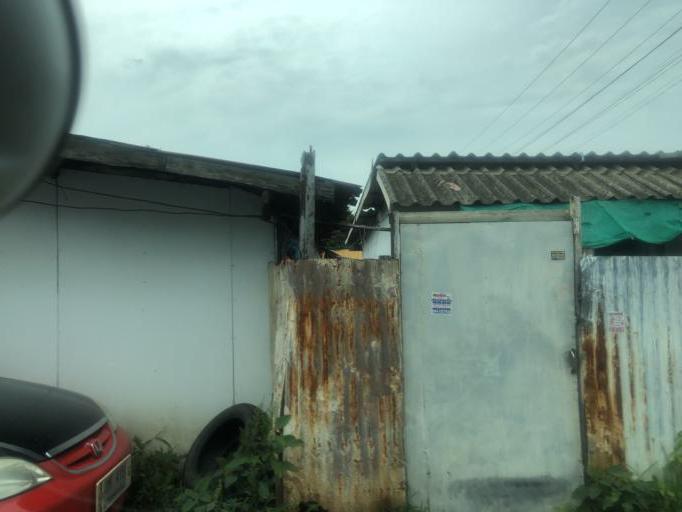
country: TH
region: Bangkok
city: Don Mueang
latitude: 13.9659
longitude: 100.6022
